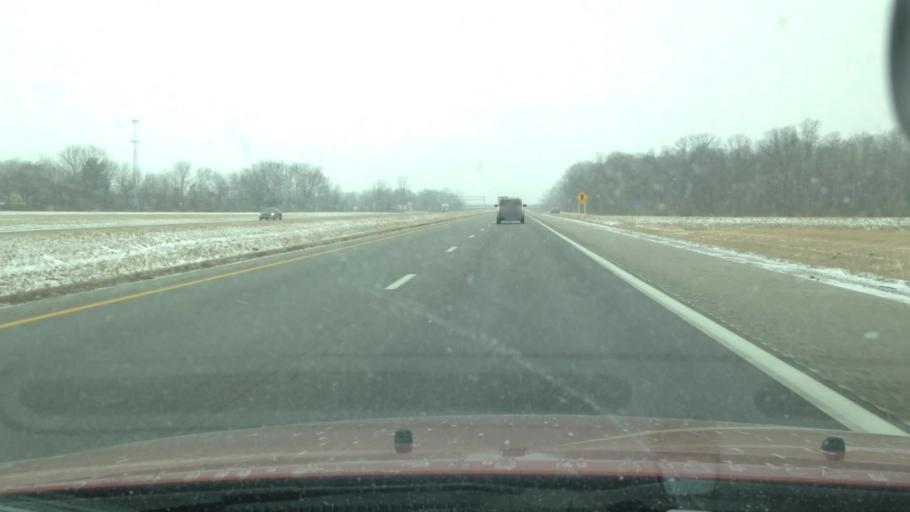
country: US
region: Ohio
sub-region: Montgomery County
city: Clayton
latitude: 39.8555
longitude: -84.3784
